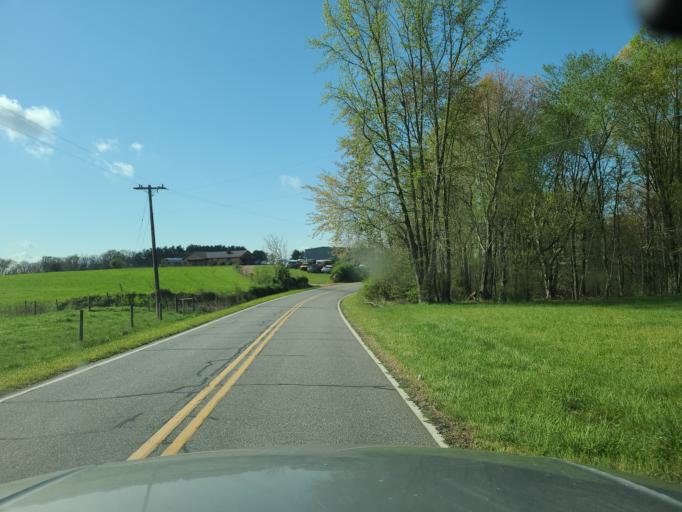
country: US
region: North Carolina
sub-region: Rutherford County
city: Forest City
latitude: 35.4123
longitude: -81.8590
